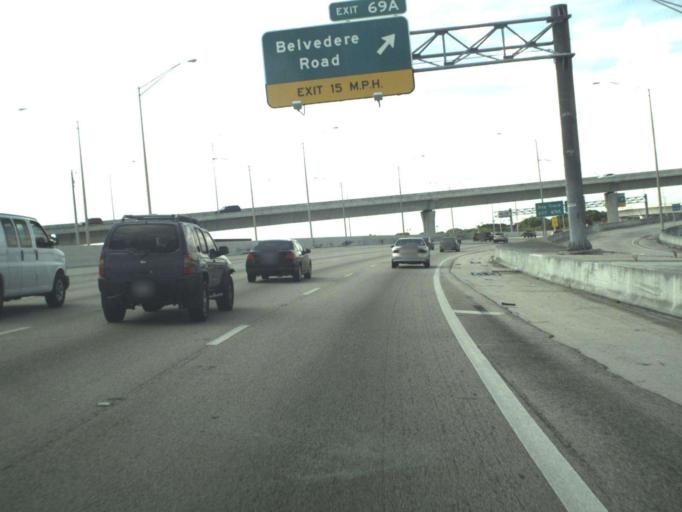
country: US
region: Florida
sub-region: Palm Beach County
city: West Palm Beach
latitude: 26.6922
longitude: -80.0675
